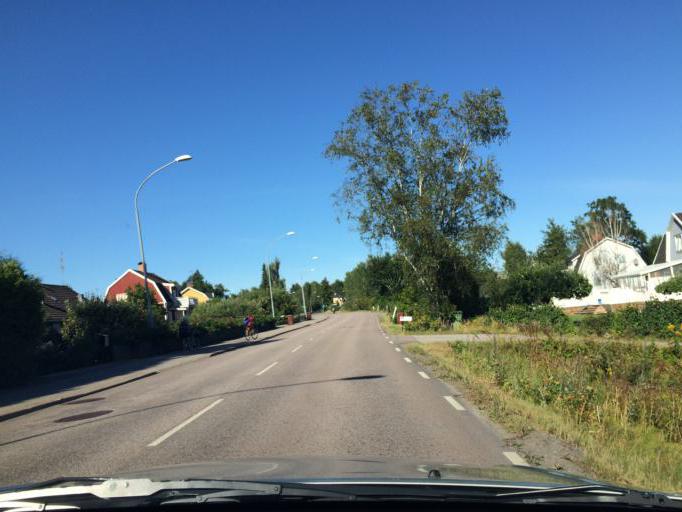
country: SE
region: Soedermanland
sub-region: Eskilstuna Kommun
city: Skogstorp
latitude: 59.3441
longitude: 16.4384
